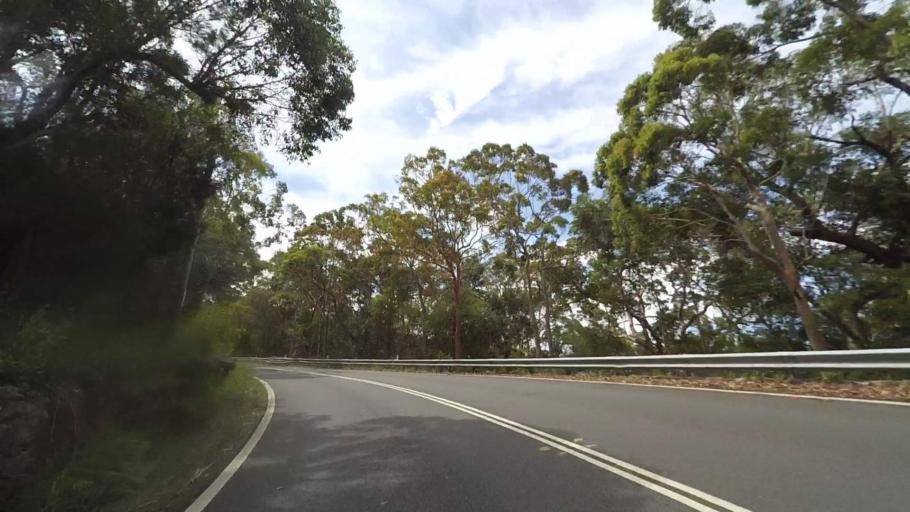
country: AU
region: New South Wales
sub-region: Sutherland Shire
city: Loftus
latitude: -34.0707
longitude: 151.0577
